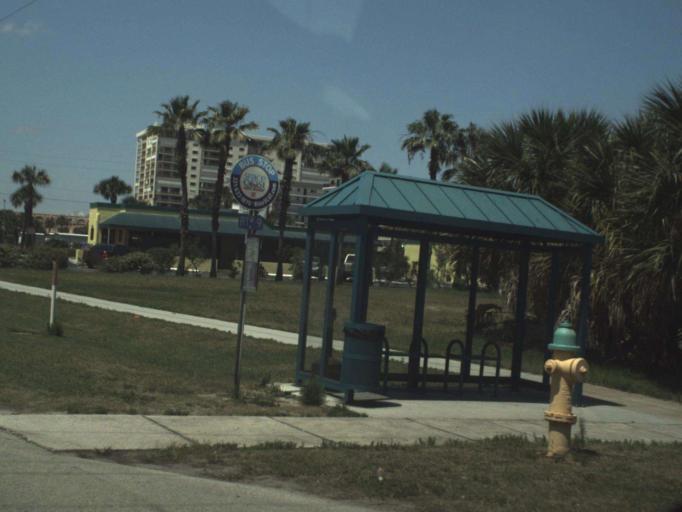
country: US
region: Florida
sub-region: Brevard County
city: Cocoa Beach
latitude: 28.3257
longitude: -80.6092
